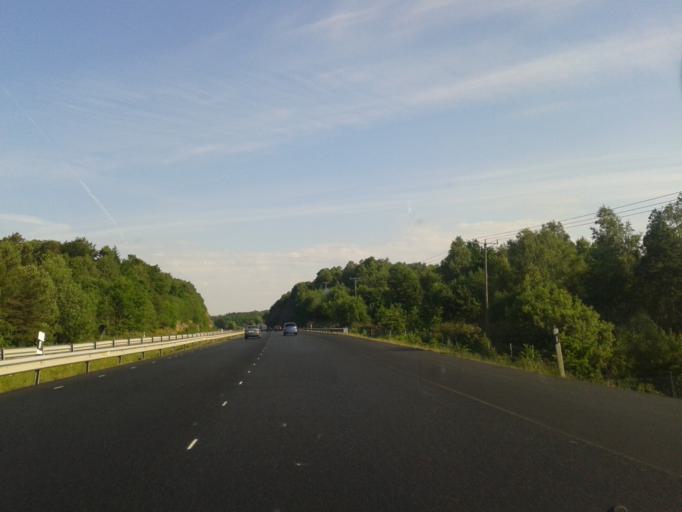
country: SE
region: Vaestra Goetaland
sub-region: Kungalvs Kommun
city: Kode
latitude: 57.9281
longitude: 11.8755
